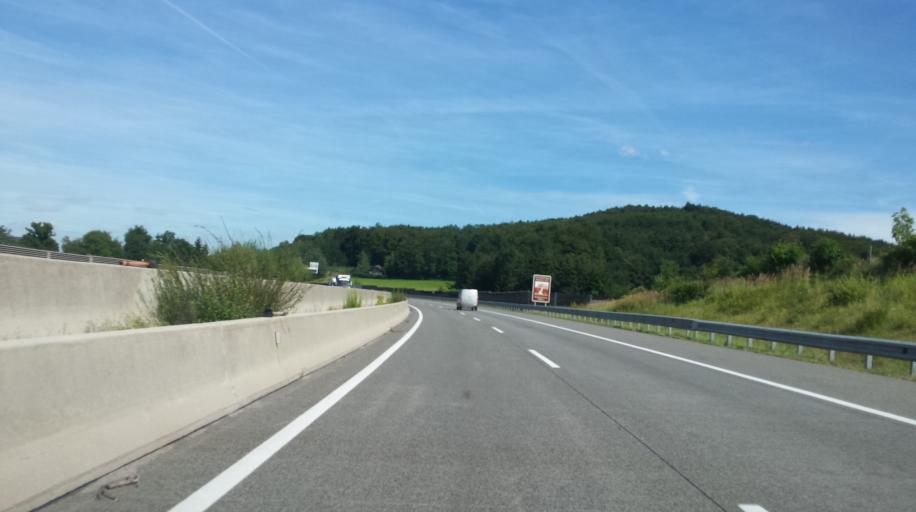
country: AT
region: Upper Austria
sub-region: Politischer Bezirk Vocklabruck
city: Aurach am Hongar
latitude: 47.9501
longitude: 13.7077
